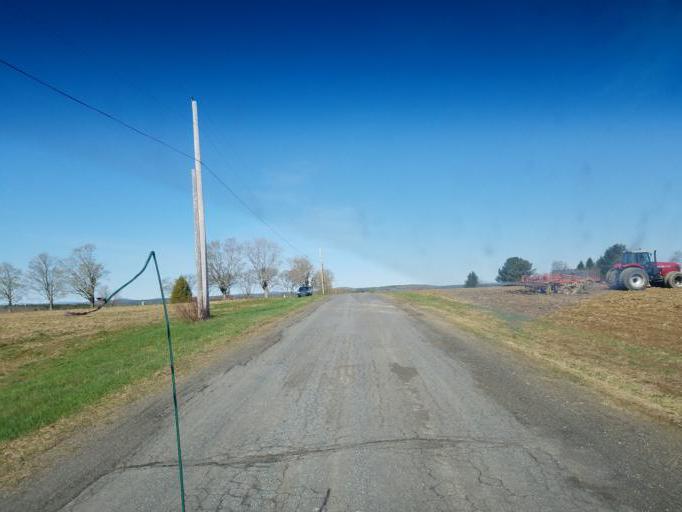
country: US
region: Maine
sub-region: Aroostook County
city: Caribou
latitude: 46.8671
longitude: -68.2054
